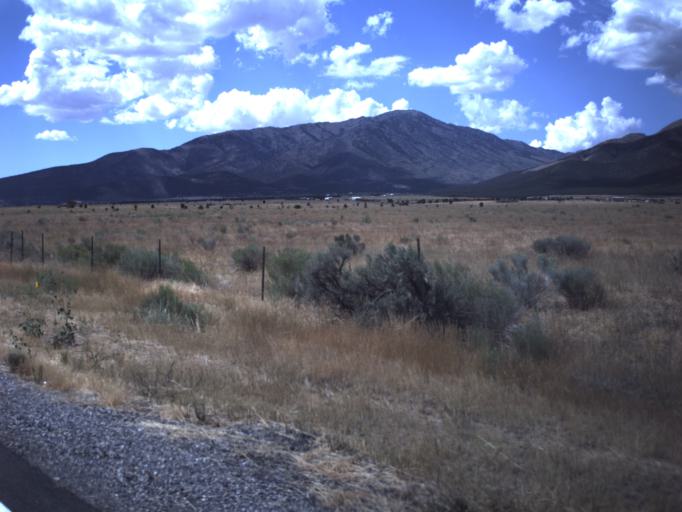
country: US
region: Utah
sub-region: Tooele County
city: Grantsville
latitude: 40.3362
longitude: -112.4901
